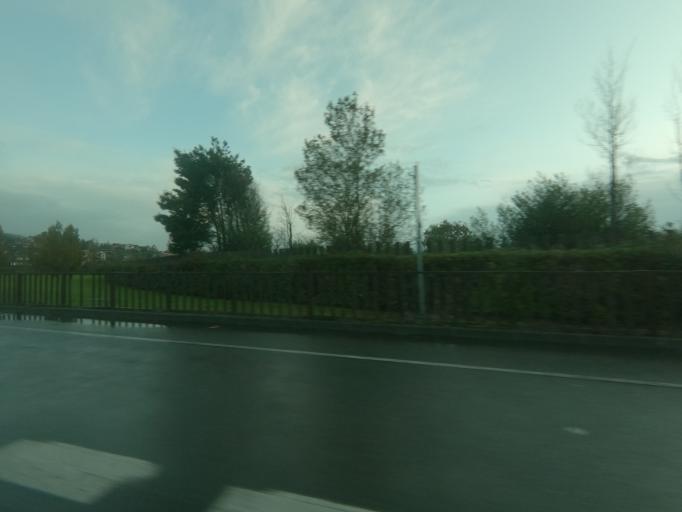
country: PT
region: Viana do Castelo
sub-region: Valenca
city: Valenca
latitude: 42.0353
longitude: -8.6554
